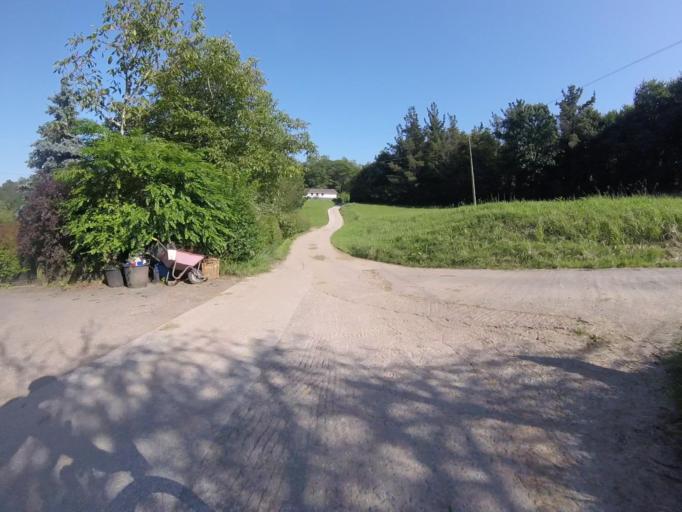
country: ES
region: Basque Country
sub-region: Provincia de Guipuzcoa
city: Astigarraga
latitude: 43.2700
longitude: -1.9328
